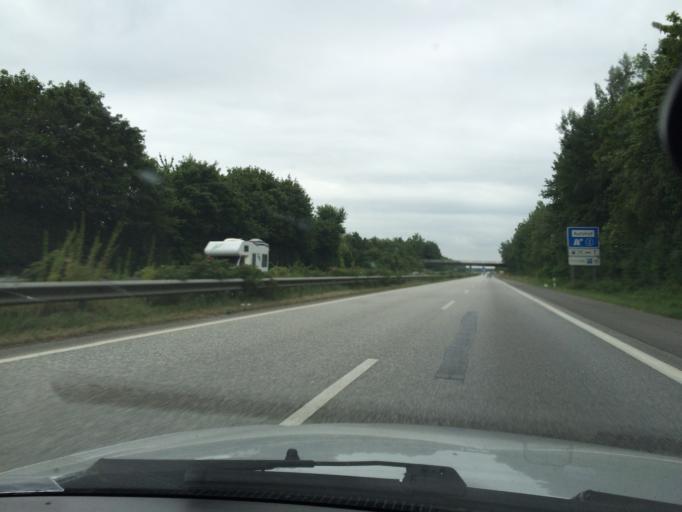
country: DE
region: Schleswig-Holstein
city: Handewitt
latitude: 54.7903
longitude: 9.3360
